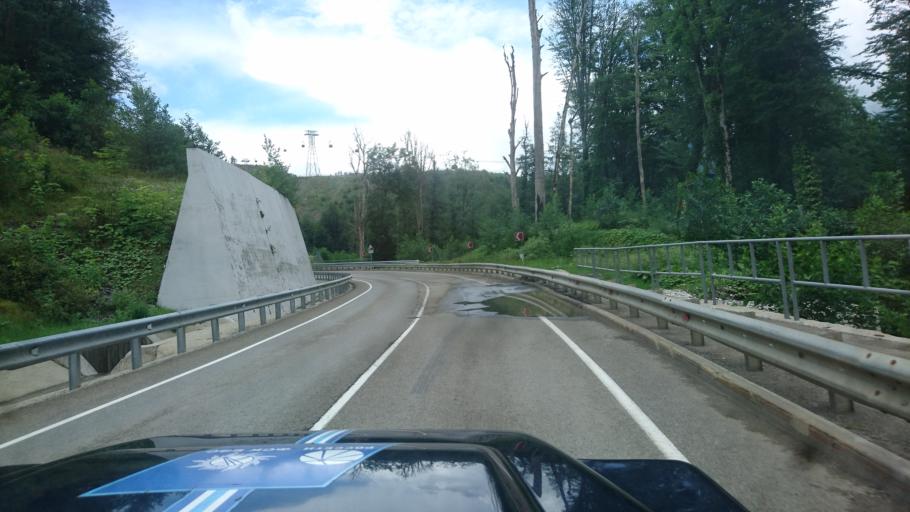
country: RU
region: Krasnodarskiy
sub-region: Sochi City
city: Krasnaya Polyana
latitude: 43.6504
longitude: 40.3322
